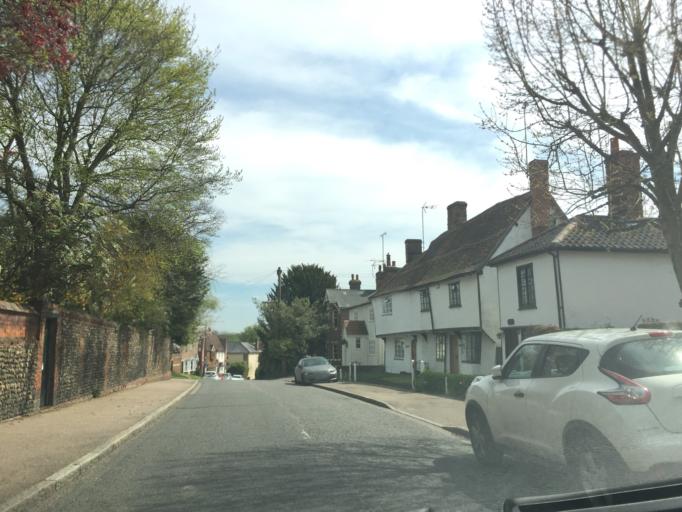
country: GB
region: England
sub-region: Essex
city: Saffron Walden
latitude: 51.9840
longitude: 0.2123
